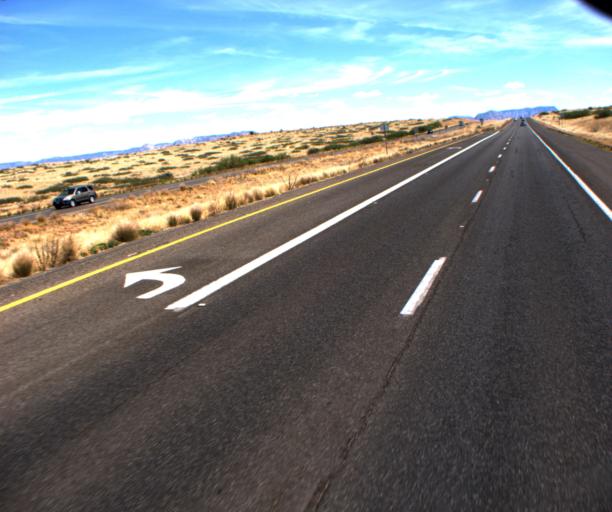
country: US
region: Arizona
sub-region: Yavapai County
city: Cornville
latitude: 34.7559
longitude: -111.9540
